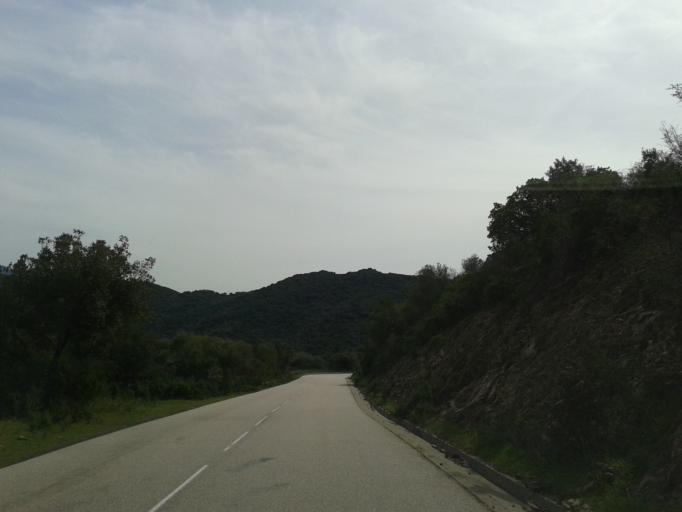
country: FR
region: Corsica
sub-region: Departement de la Haute-Corse
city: Monticello
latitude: 42.6516
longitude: 9.1070
